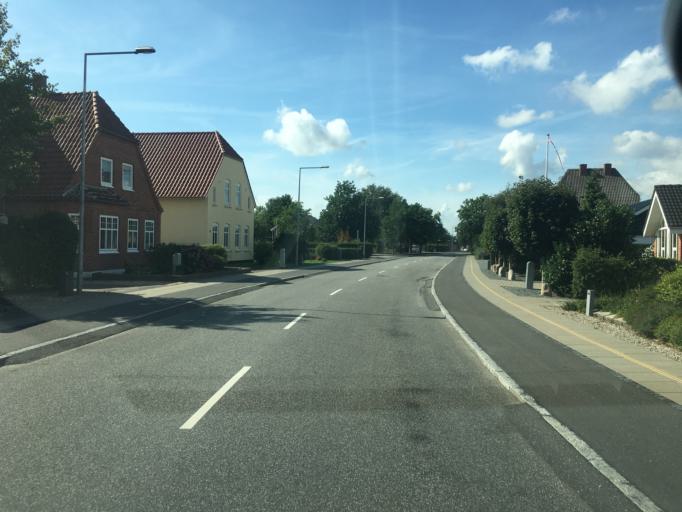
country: DK
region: South Denmark
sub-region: Tonder Kommune
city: Tonder
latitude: 54.9358
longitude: 8.8527
